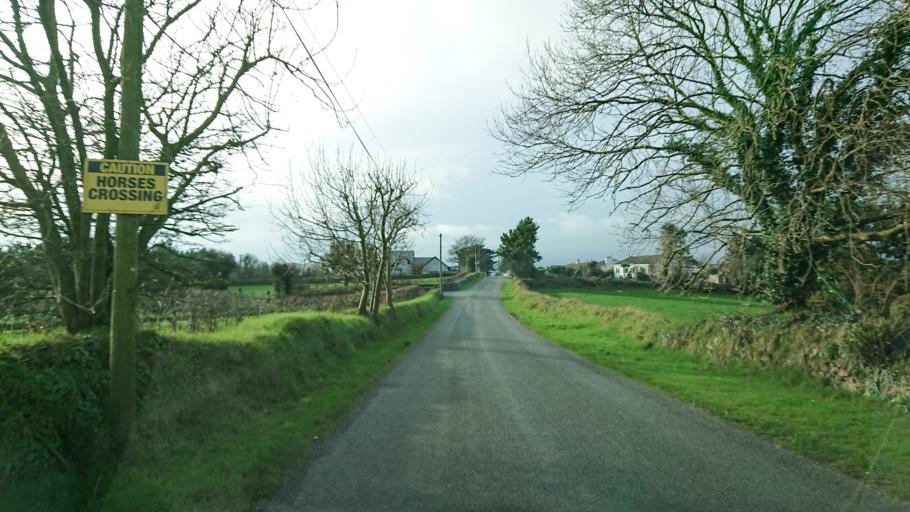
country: IE
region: Munster
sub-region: Waterford
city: Tra Mhor
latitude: 52.1694
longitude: -7.1829
